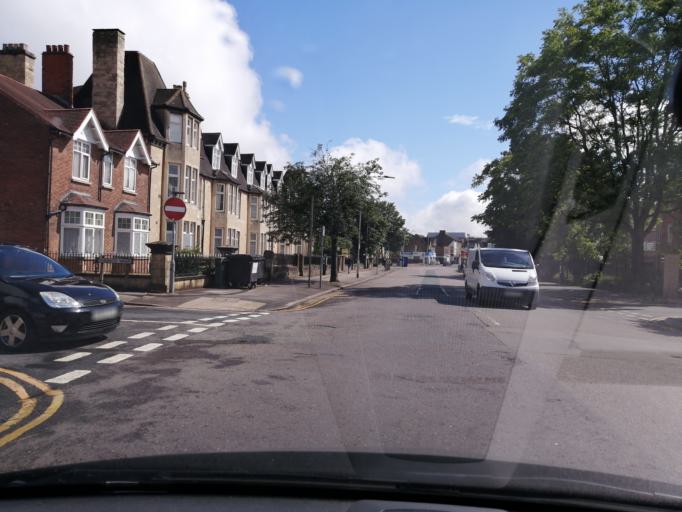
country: GB
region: England
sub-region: Peterborough
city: Peterborough
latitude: 52.5786
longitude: -0.2434
